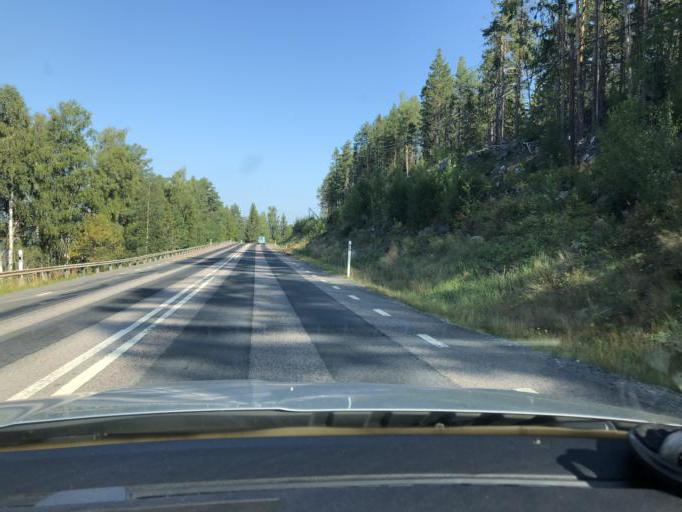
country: SE
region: Vaesternorrland
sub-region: Kramfors Kommun
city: Kramfors
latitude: 62.8886
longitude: 17.9058
